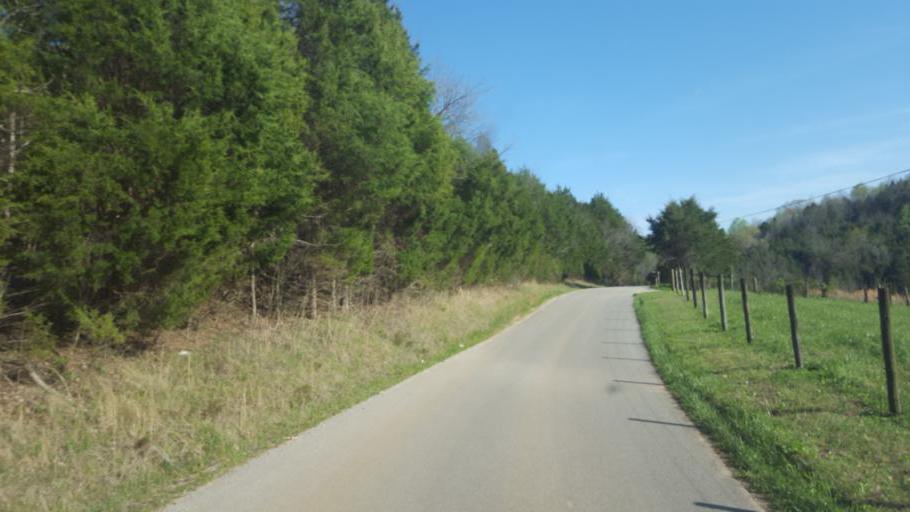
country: US
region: Kentucky
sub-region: Barren County
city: Cave City
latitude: 37.1802
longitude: -86.0075
